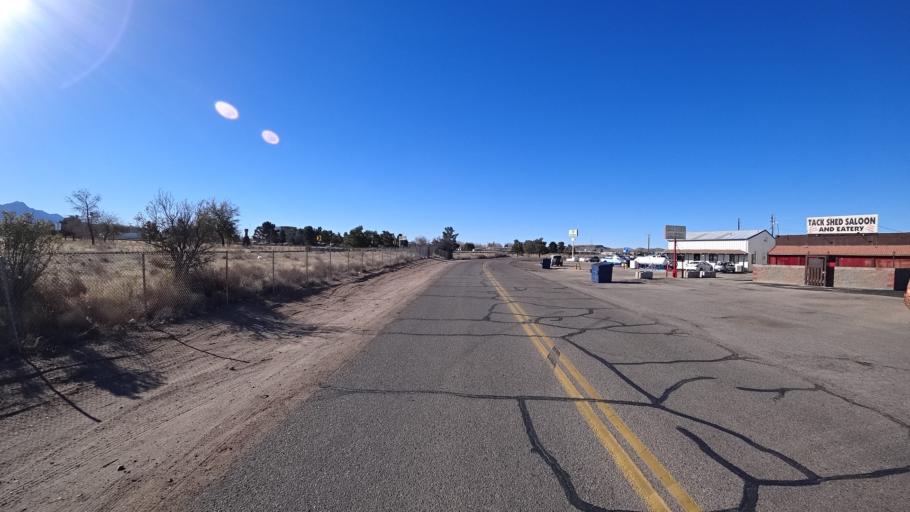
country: US
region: Arizona
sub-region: Mohave County
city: Kingman
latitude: 35.2186
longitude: -114.0140
